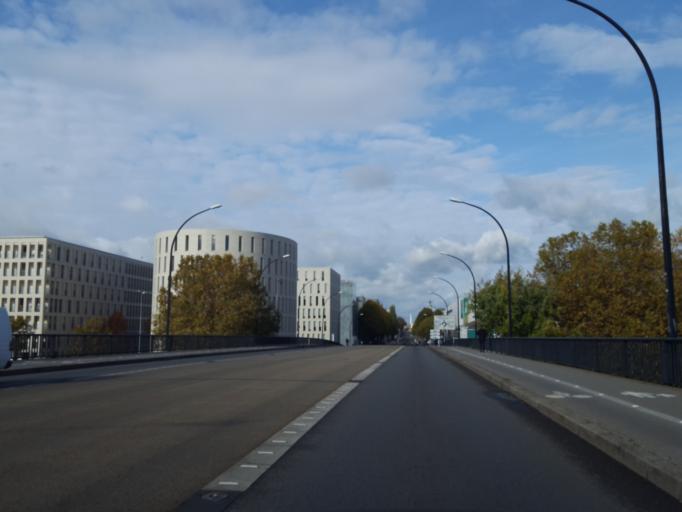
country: FR
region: Pays de la Loire
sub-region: Departement de la Loire-Atlantique
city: Nantes
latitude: 47.2103
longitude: -1.5422
